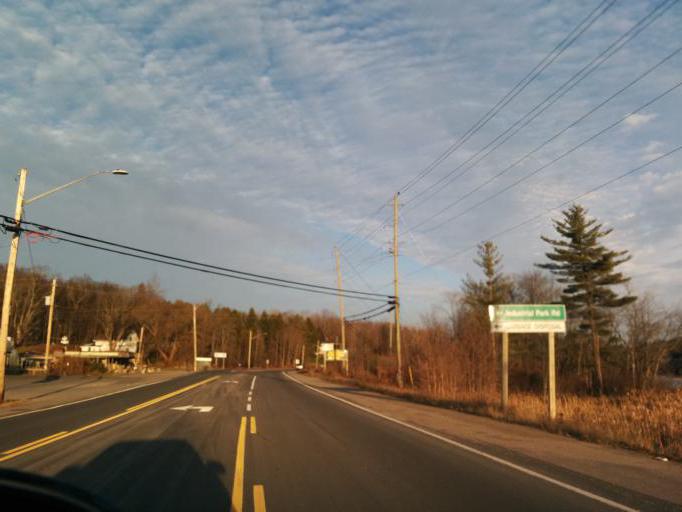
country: CA
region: Ontario
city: Bancroft
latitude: 45.0467
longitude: -78.5326
